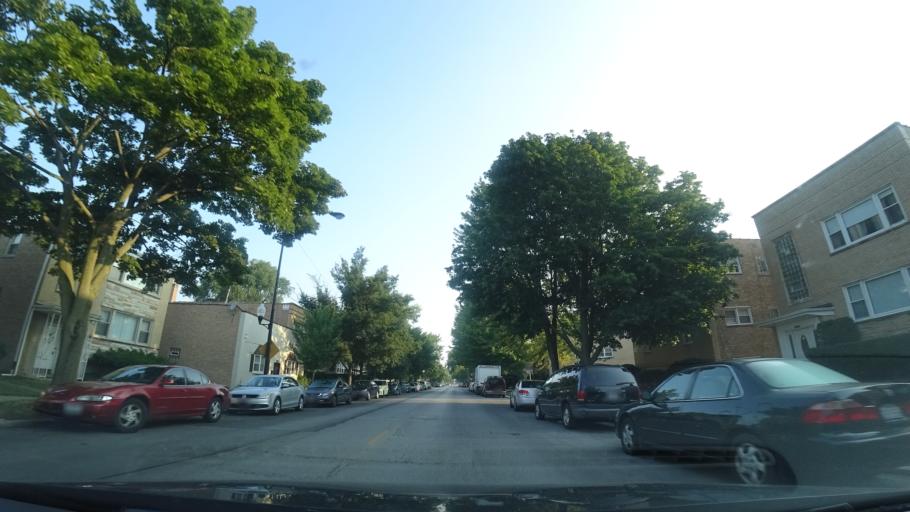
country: US
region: Illinois
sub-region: Cook County
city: Lincolnwood
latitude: 42.0017
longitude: -87.6999
